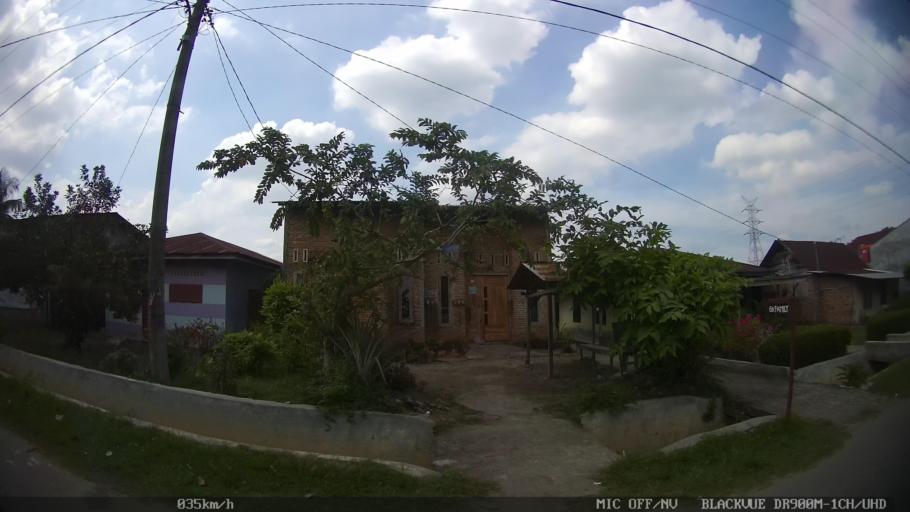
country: ID
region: North Sumatra
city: Binjai
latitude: 3.6354
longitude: 98.5053
